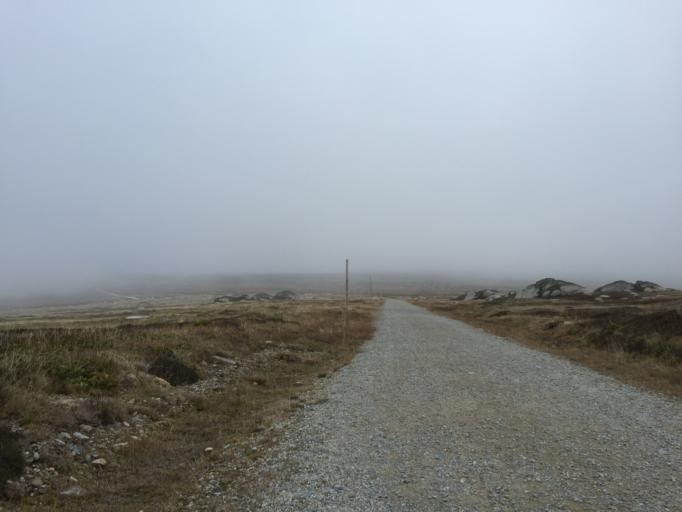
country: AU
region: New South Wales
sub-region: Snowy River
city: Jindabyne
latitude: -36.4556
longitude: 148.2888
